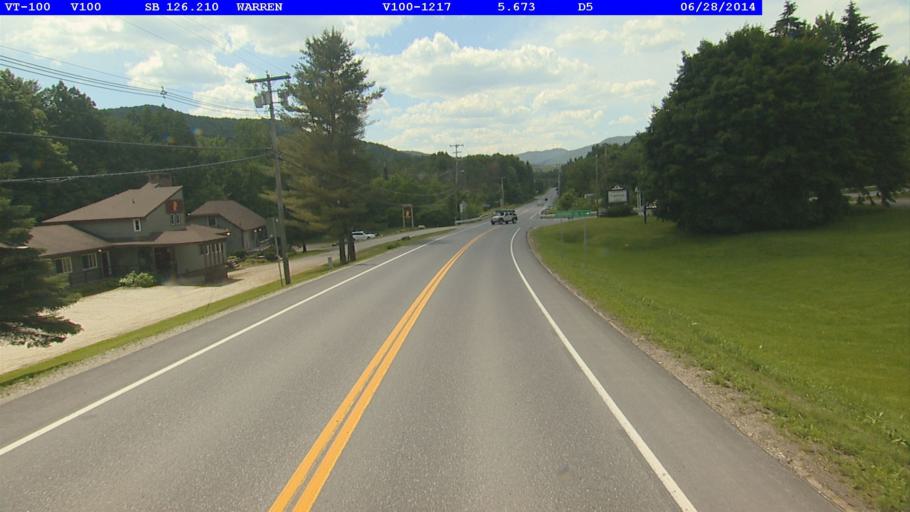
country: US
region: Vermont
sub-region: Washington County
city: Northfield
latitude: 44.1380
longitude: -72.8458
